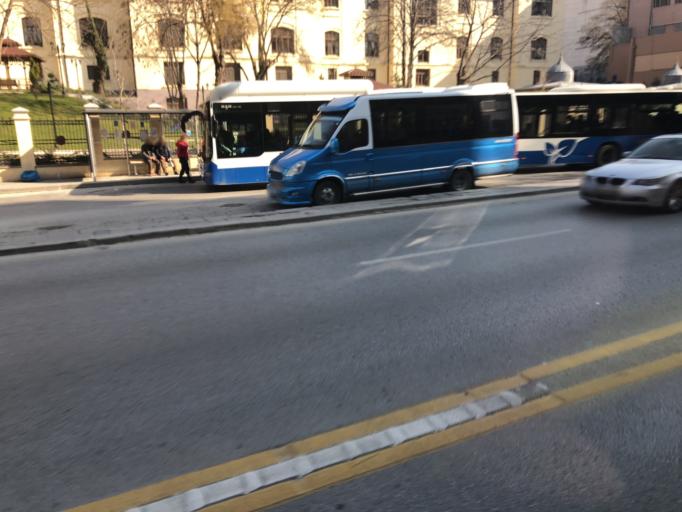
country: TR
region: Ankara
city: Ankara
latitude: 39.9437
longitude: 32.8547
